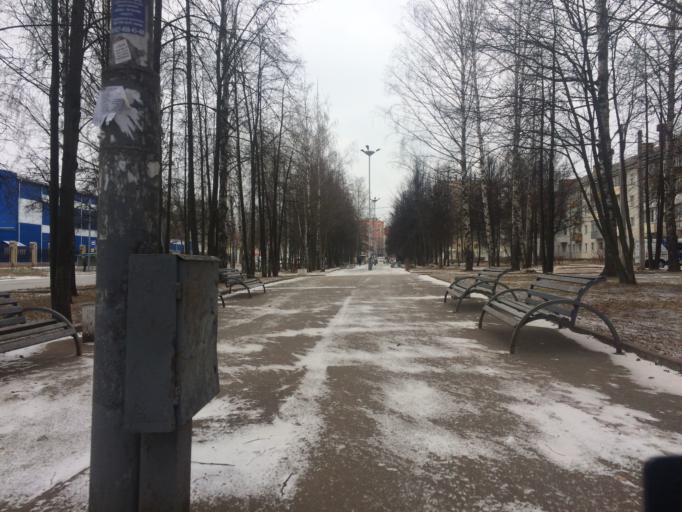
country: RU
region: Mariy-El
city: Yoshkar-Ola
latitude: 56.6427
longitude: 47.8725
